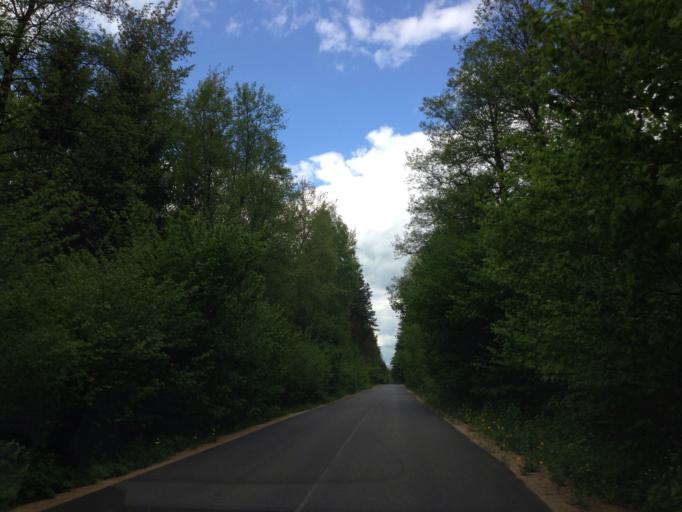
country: PL
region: Podlasie
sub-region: Powiat grajewski
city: Radzilow
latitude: 53.3322
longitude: 22.5996
